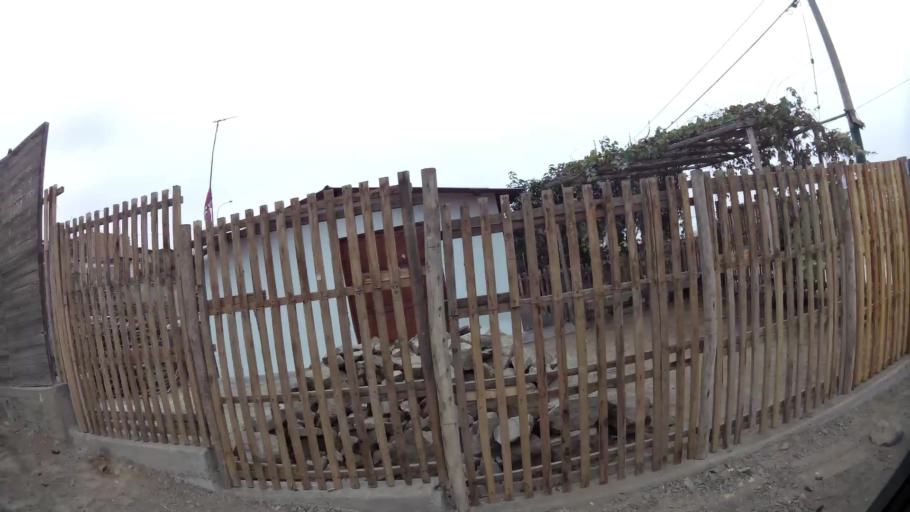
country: PE
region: Lima
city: Ventanilla
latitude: -11.8452
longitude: -77.1444
